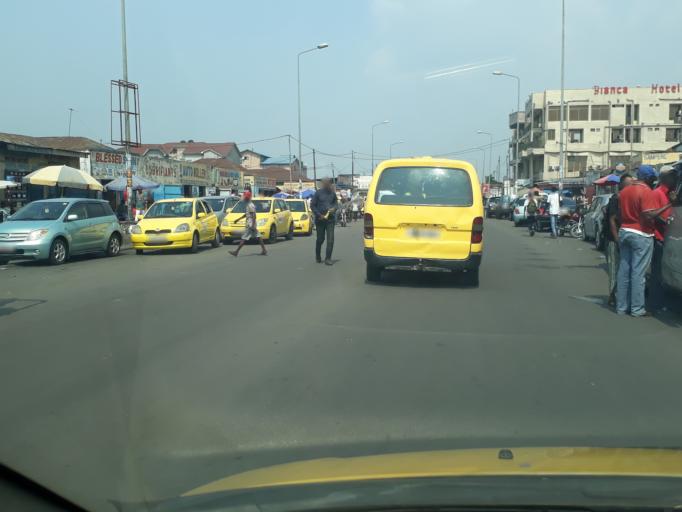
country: CD
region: Kinshasa
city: Kinshasa
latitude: -4.3400
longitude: 15.3108
